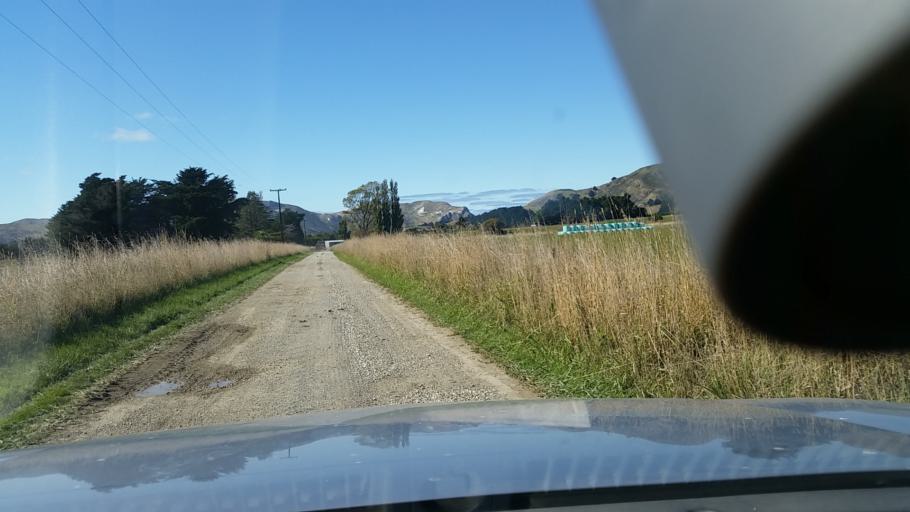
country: NZ
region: Marlborough
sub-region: Marlborough District
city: Blenheim
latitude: -41.8247
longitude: 174.1249
